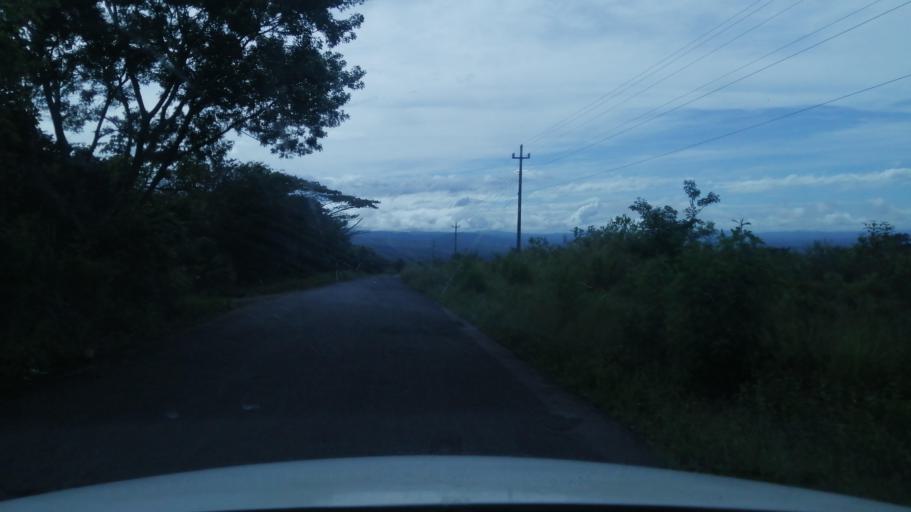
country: PA
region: Chiriqui
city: Potrerillos Abajo
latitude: 8.6716
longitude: -82.4364
